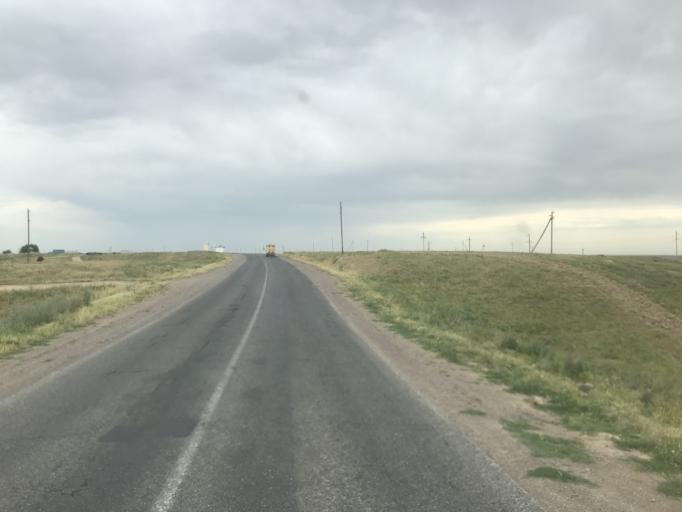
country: UZ
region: Toshkent
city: Yangiyul
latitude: 41.2979
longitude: 68.8501
